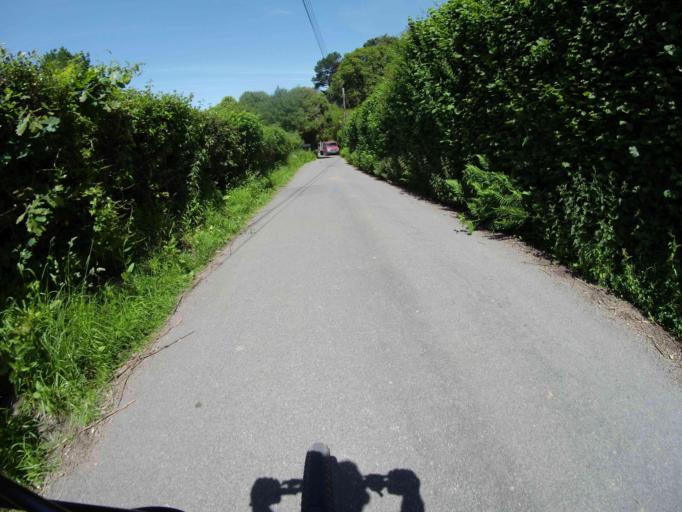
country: GB
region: England
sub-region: Devon
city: Bovey Tracey
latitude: 50.6170
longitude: -3.7135
